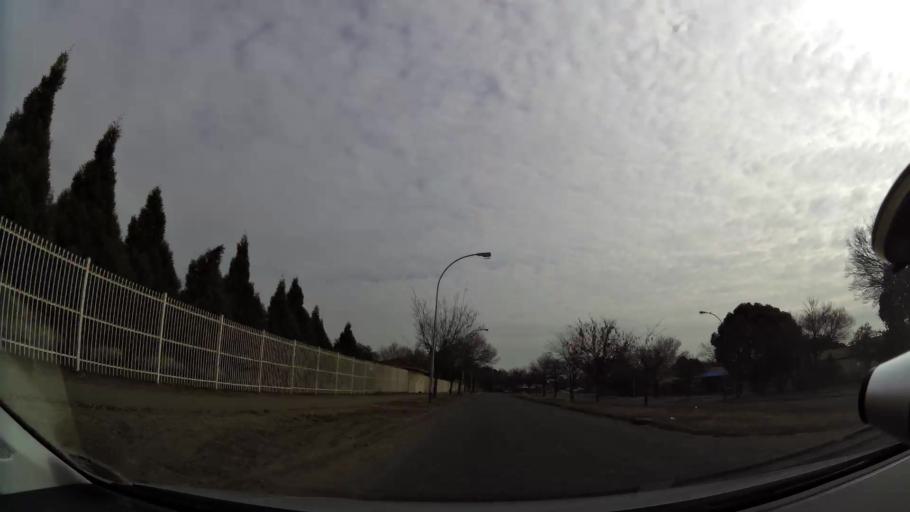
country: ZA
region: Orange Free State
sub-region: Mangaung Metropolitan Municipality
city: Bloemfontein
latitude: -29.1250
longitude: 26.1990
